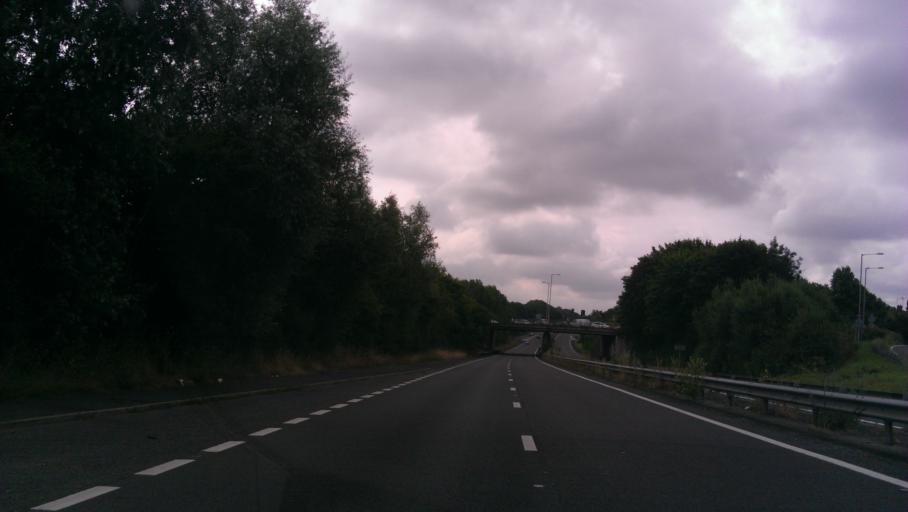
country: GB
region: England
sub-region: Kent
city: Canterbury
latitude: 51.2711
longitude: 1.0594
